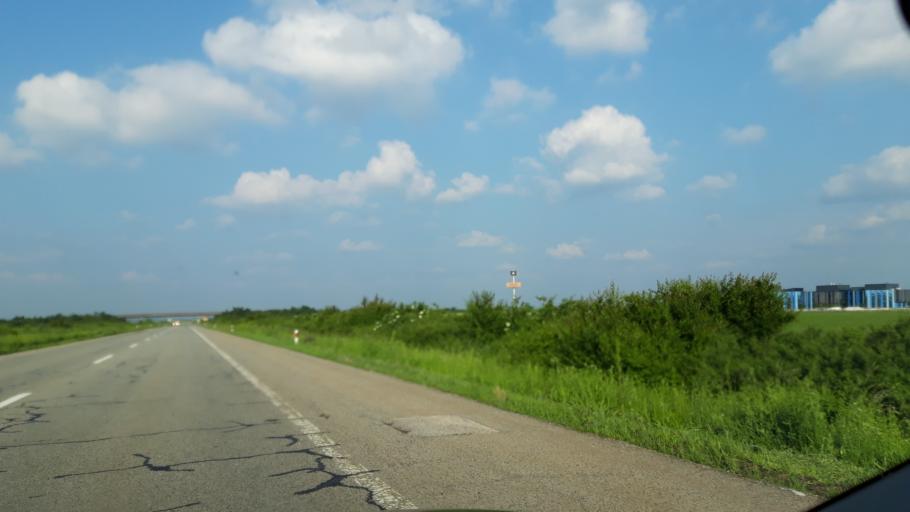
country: RS
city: Beska
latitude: 45.0968
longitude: 20.0866
